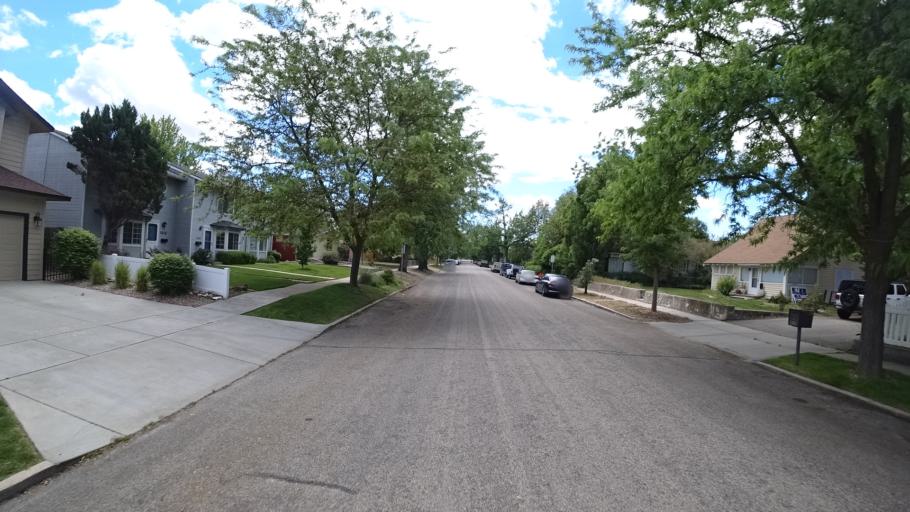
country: US
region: Idaho
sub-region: Ada County
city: Boise
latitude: 43.5966
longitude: -116.1985
